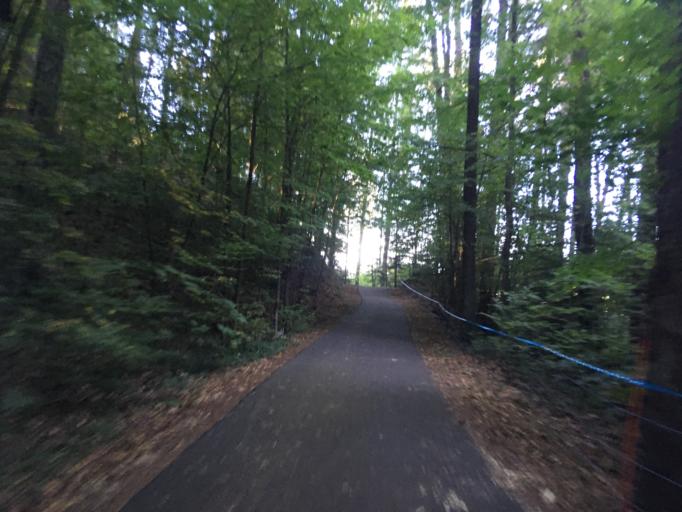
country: PL
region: Lubusz
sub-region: Powiat zarski
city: Leknica
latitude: 51.6022
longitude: 14.7573
